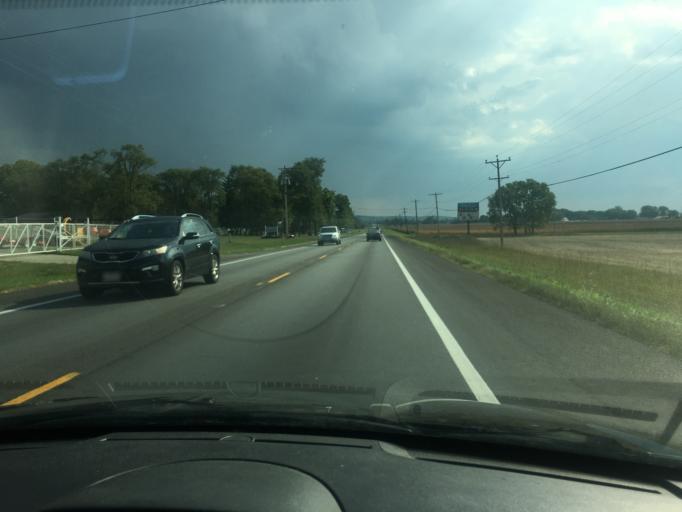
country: US
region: Ohio
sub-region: Champaign County
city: Urbana
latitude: 40.0566
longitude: -83.7782
